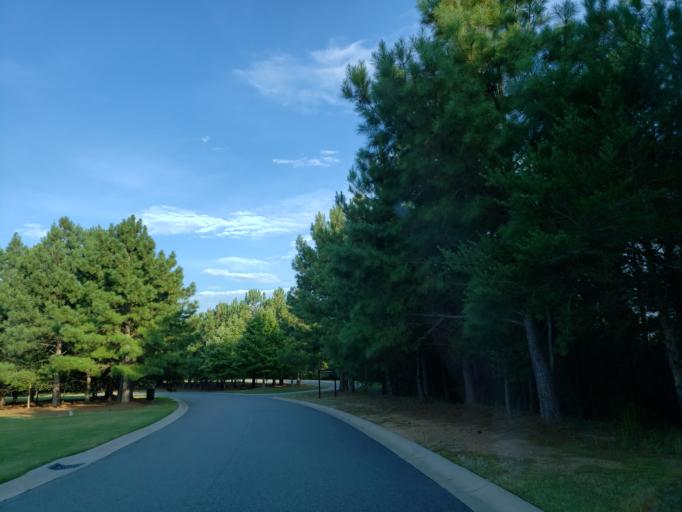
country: US
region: Georgia
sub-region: Cherokee County
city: Canton
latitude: 34.2341
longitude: -84.5796
